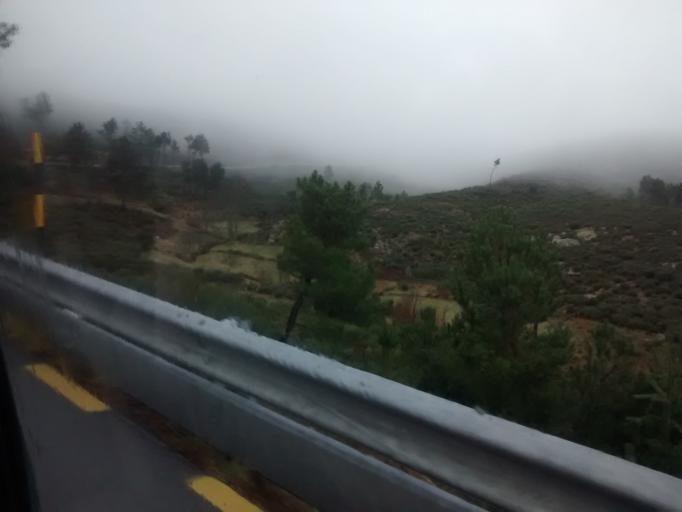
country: PT
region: Guarda
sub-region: Seia
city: Seia
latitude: 40.3988
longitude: -7.6501
